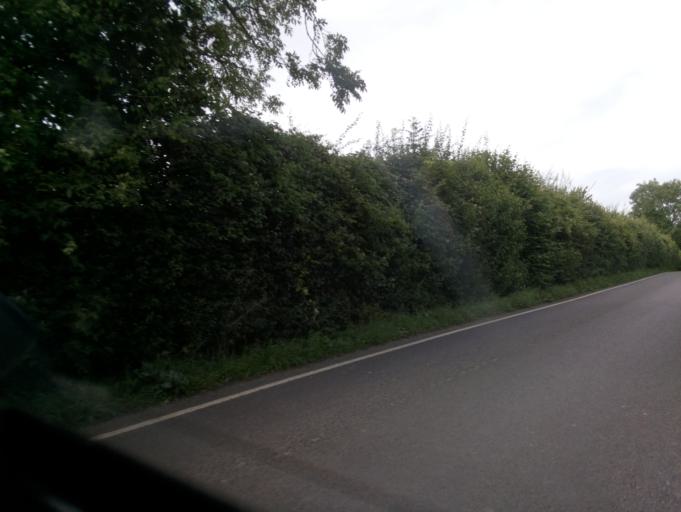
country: GB
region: England
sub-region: Somerset
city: Street
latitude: 51.0859
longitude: -2.6942
